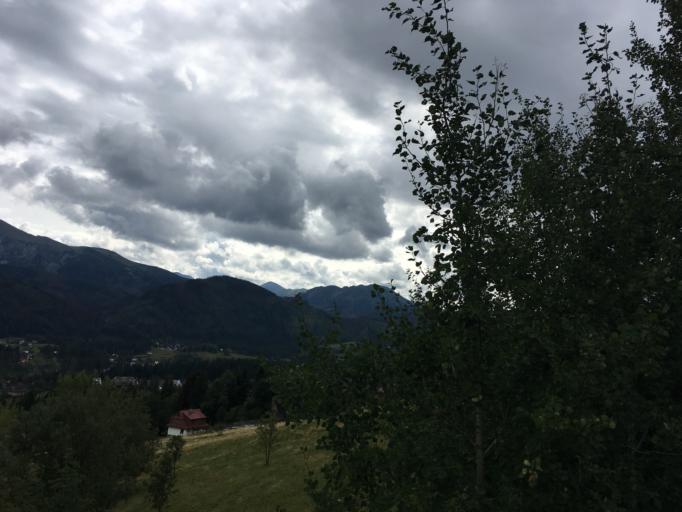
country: PL
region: Lesser Poland Voivodeship
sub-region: Powiat tatrzanski
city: Koscielisko
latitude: 49.2965
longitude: 19.9126
